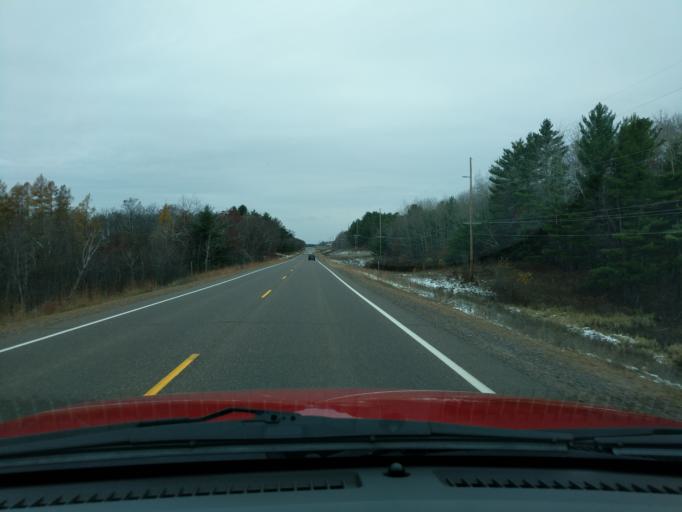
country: US
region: Wisconsin
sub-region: Burnett County
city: Siren
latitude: 45.8088
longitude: -92.1880
